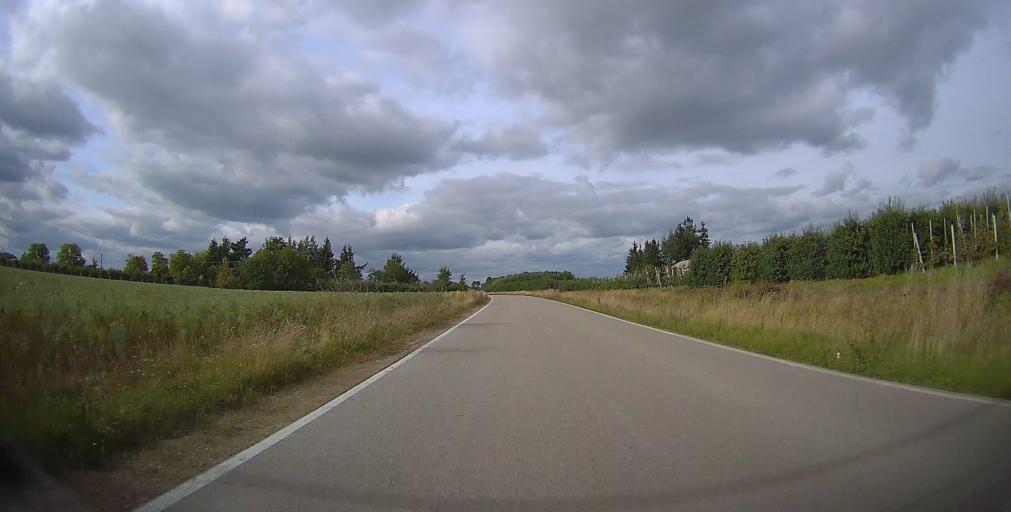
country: PL
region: Masovian Voivodeship
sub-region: Powiat grojecki
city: Goszczyn
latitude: 51.7563
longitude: 20.9020
